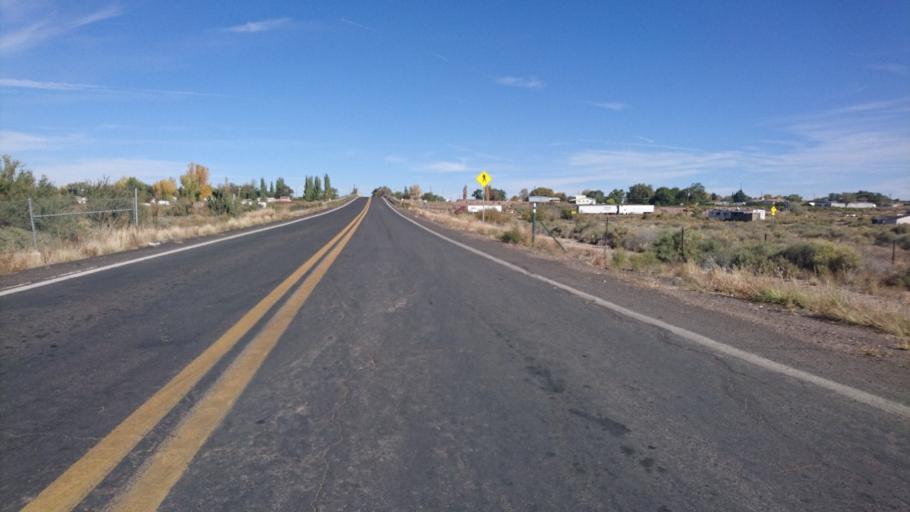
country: US
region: Arizona
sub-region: Navajo County
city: Joseph City
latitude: 34.9522
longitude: -110.3313
